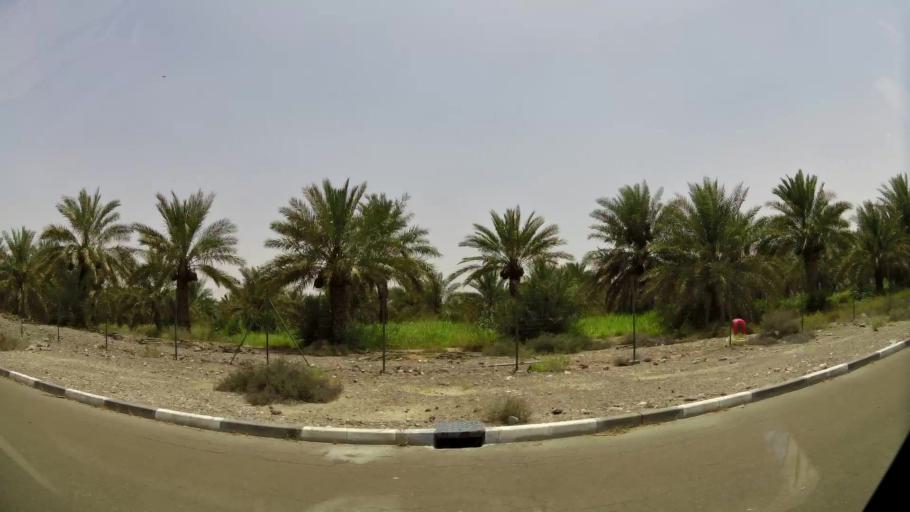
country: AE
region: Abu Dhabi
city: Al Ain
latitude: 24.2011
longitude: 55.7042
